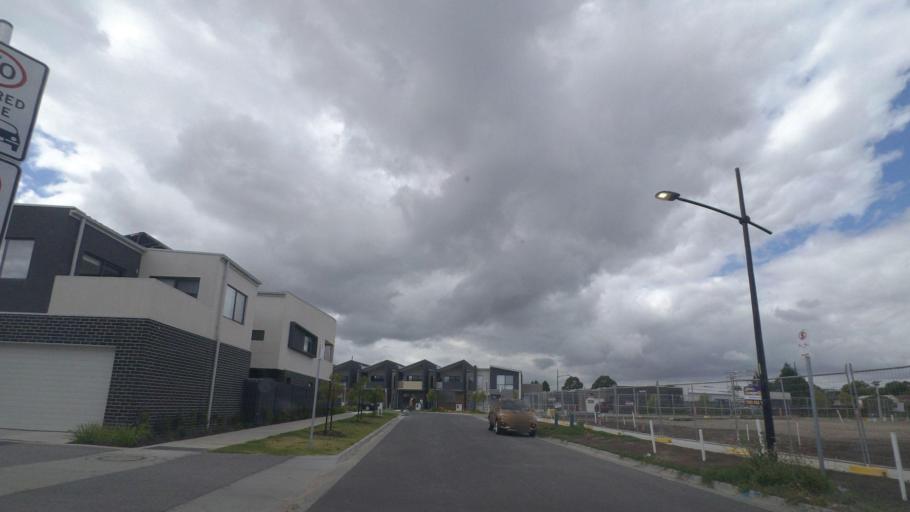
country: AU
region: Victoria
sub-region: Knox
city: Scoresby
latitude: -37.9151
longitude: 145.2296
